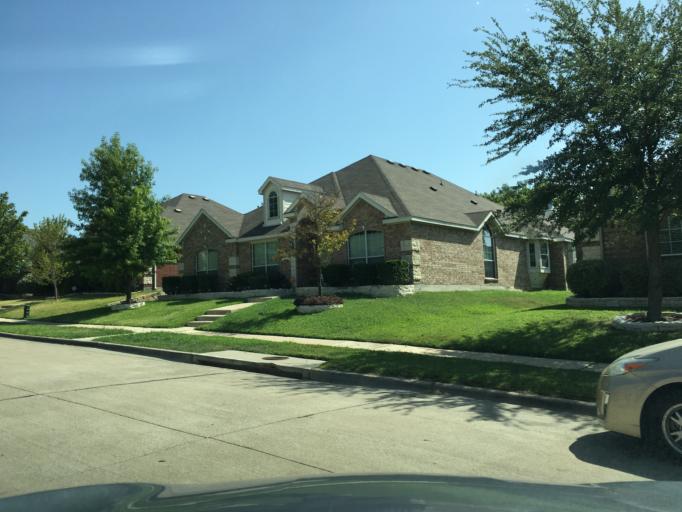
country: US
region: Texas
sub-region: Dallas County
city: Garland
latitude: 32.8897
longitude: -96.6113
